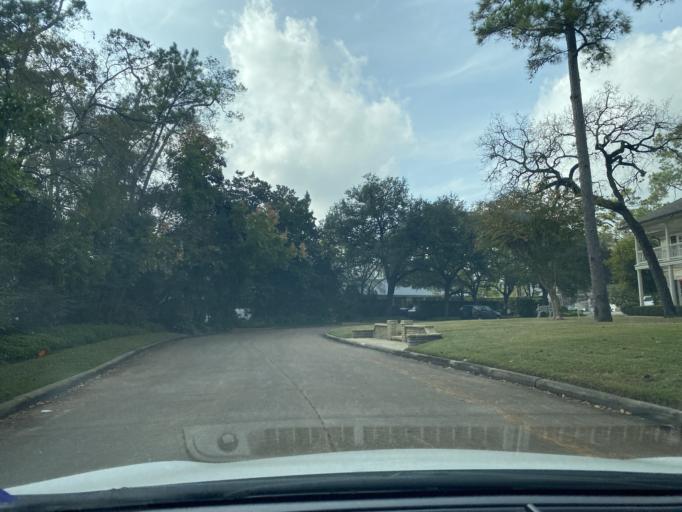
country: US
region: Texas
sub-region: Harris County
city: Hunters Creek Village
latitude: 29.7658
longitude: -95.4667
